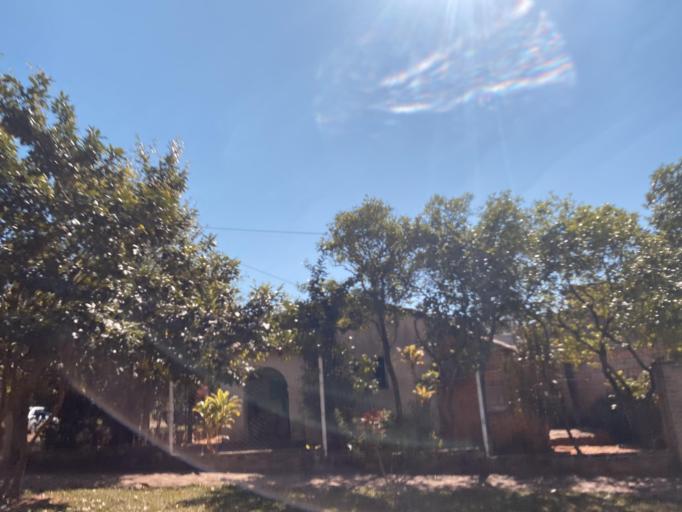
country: PY
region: Misiones
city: San Juan Bautista
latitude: -26.6660
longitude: -57.1526
